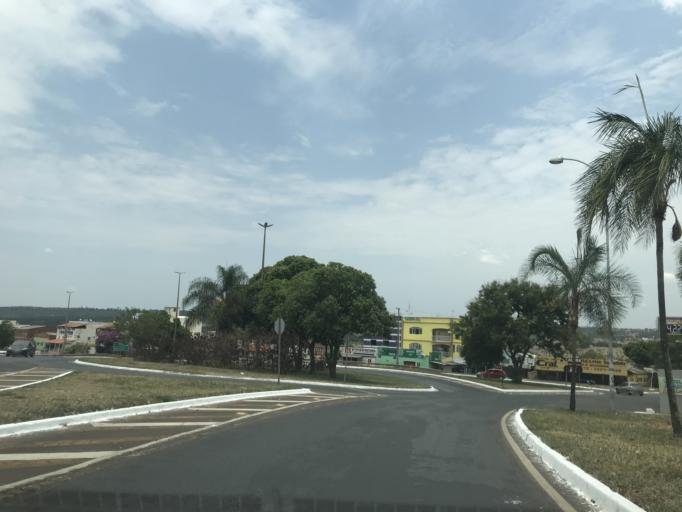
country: BR
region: Federal District
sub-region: Brasilia
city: Brasilia
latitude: -15.6605
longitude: -47.8061
